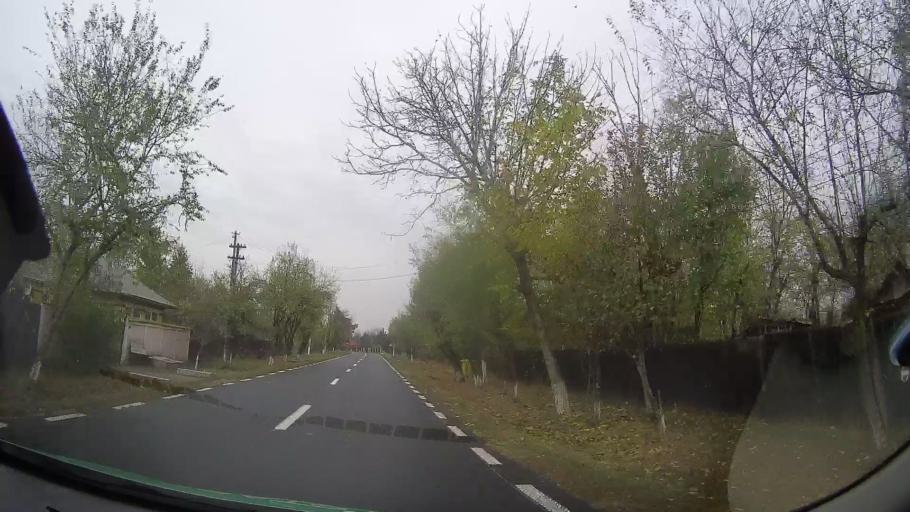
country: RO
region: Ilfov
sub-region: Comuna Nuci
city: Nuci
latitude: 44.7216
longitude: 26.2953
